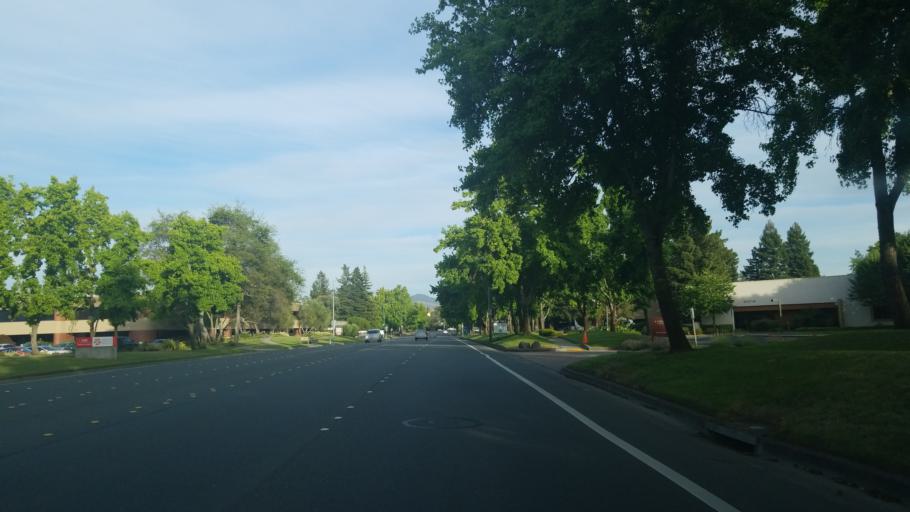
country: US
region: California
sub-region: Sonoma County
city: Santa Rosa
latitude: 38.4498
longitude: -122.7337
